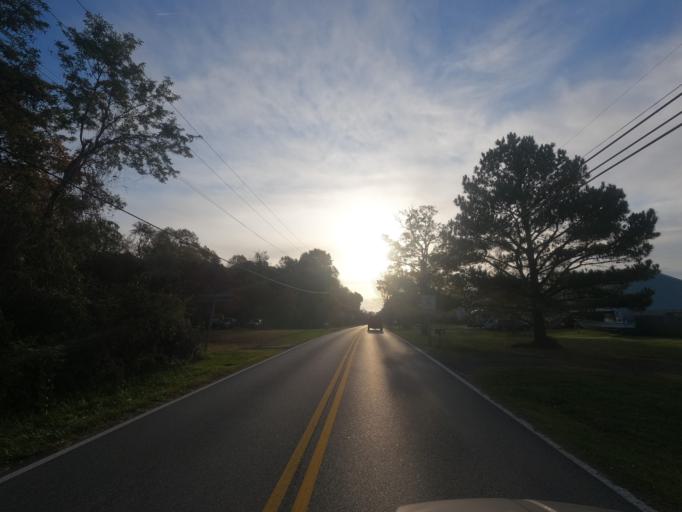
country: US
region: Maryland
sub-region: Calvert County
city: Lusby
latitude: 38.3881
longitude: -76.4299
